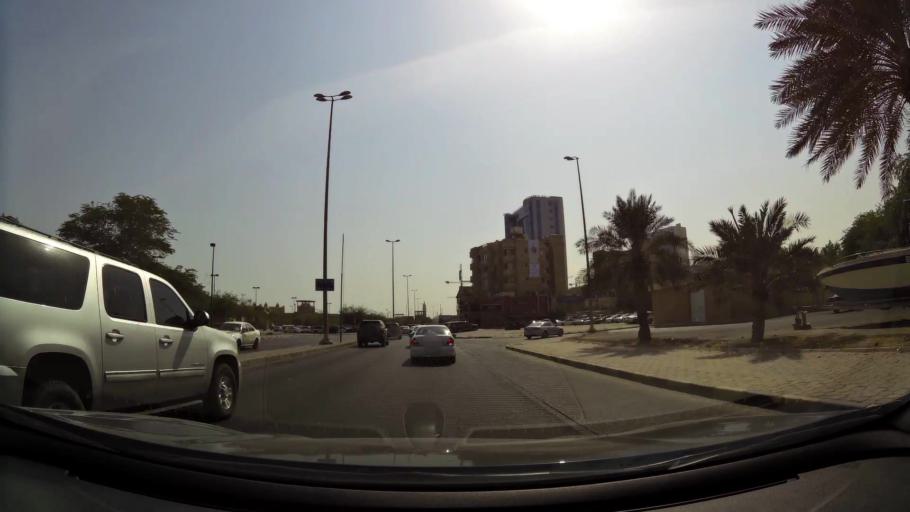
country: KW
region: Al Ahmadi
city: Al Fahahil
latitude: 29.0839
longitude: 48.1397
